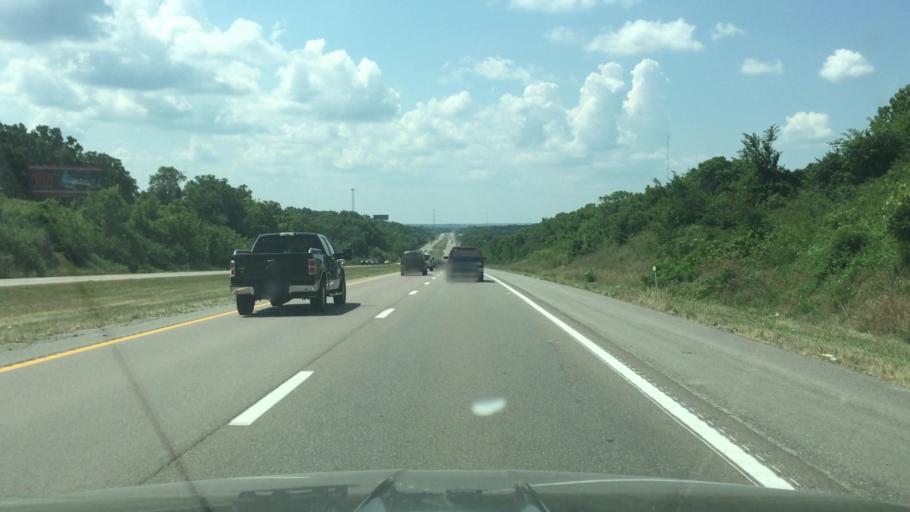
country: US
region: Missouri
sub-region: Miller County
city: Eldon
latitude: 38.2925
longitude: -92.5807
